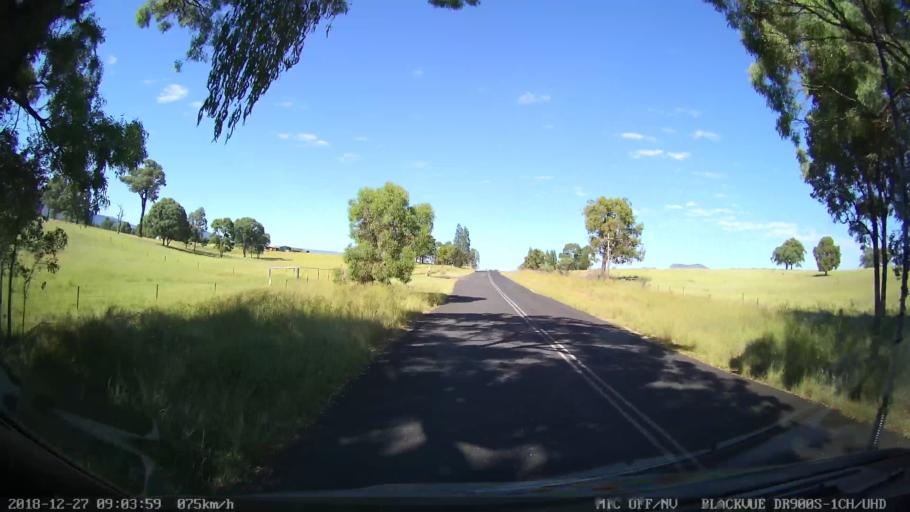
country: AU
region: New South Wales
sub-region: Lithgow
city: Portland
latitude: -33.1079
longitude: 150.1955
